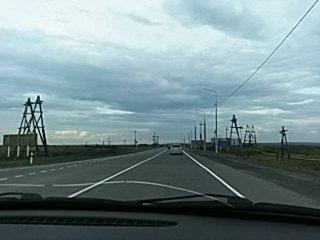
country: RU
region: Krasnoyarskiy
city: Kayyerkan
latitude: 69.3727
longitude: 87.3665
